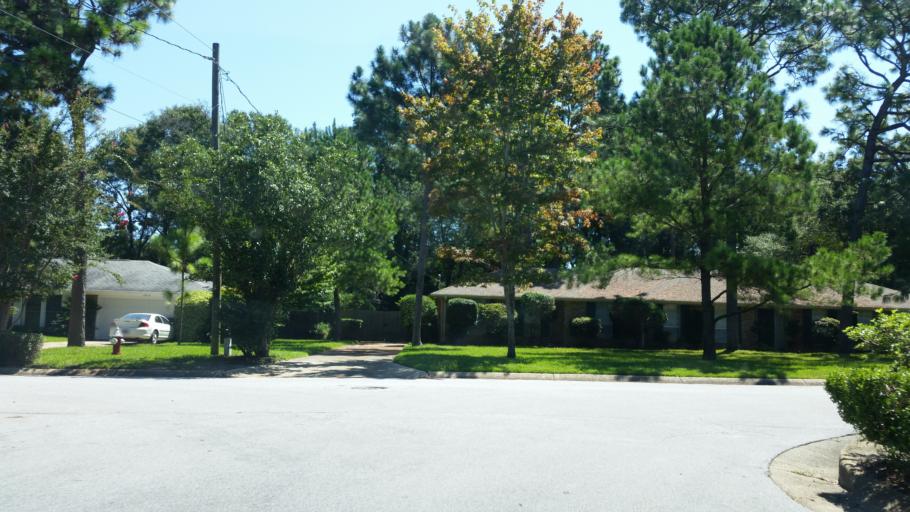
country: US
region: Florida
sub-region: Escambia County
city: Ferry Pass
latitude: 30.5074
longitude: -87.1863
